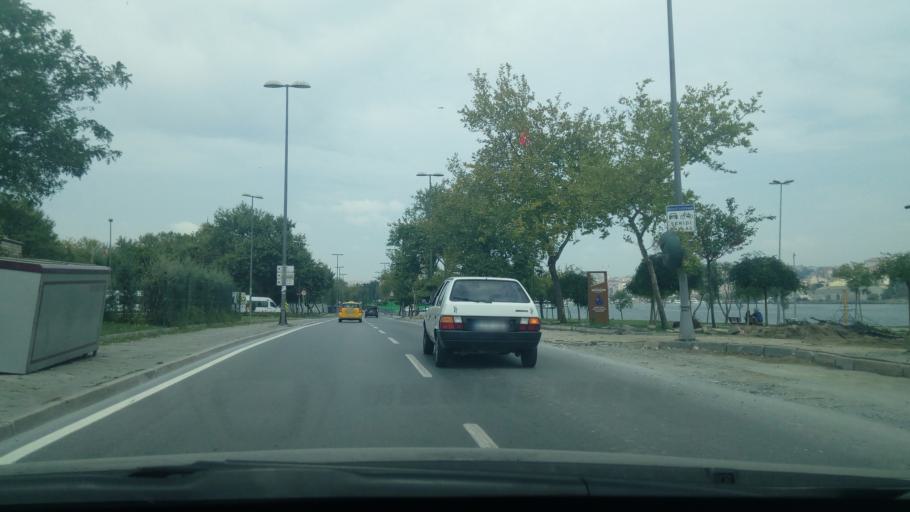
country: TR
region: Istanbul
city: Istanbul
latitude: 41.0300
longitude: 28.9515
